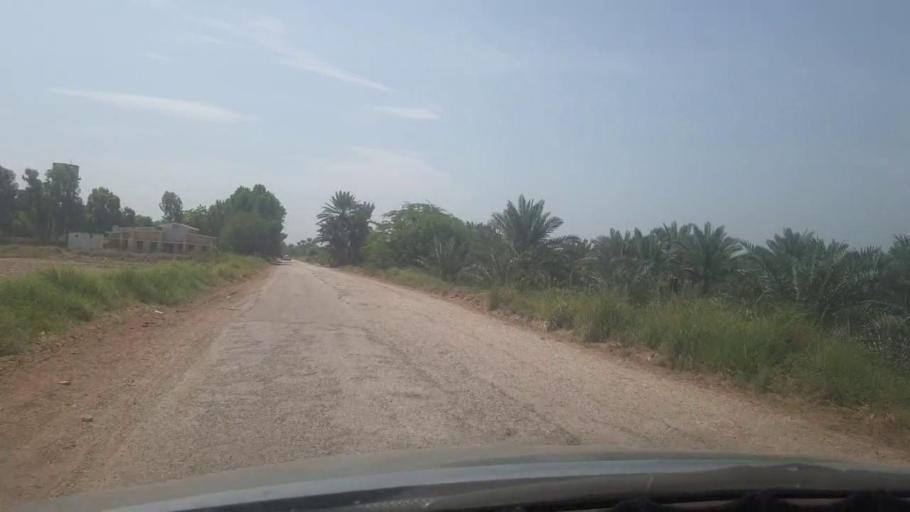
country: PK
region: Sindh
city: Bozdar
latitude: 27.1993
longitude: 68.5847
